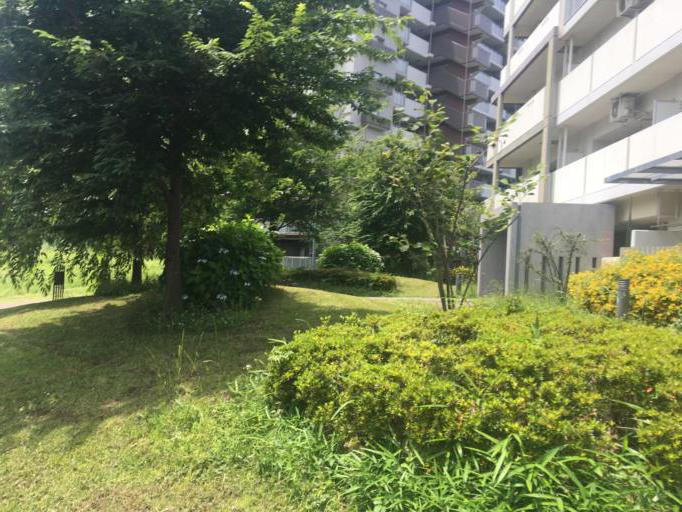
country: JP
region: Tokyo
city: Tanashicho
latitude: 35.7455
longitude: 139.5365
